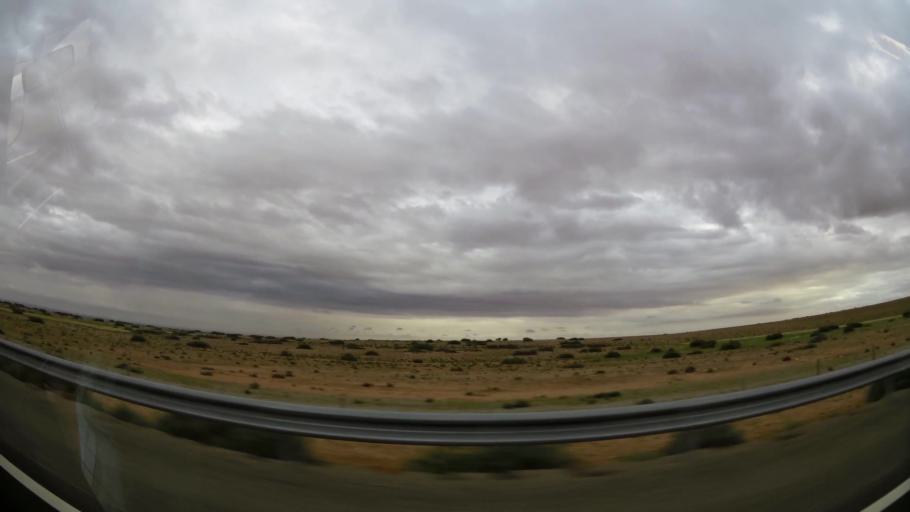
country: MA
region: Taza-Al Hoceima-Taounate
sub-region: Taza
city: Guercif
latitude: 34.3054
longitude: -3.6470
